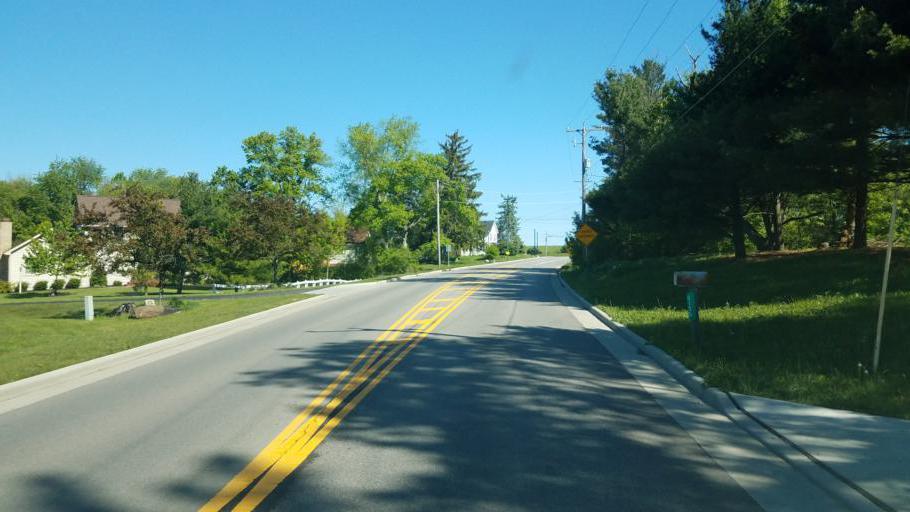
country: US
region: Ohio
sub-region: Delaware County
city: Lewis Center
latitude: 40.1801
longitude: -82.9560
